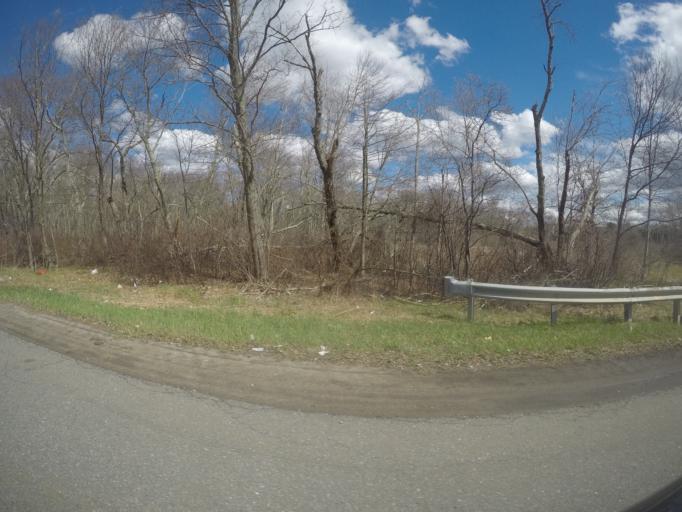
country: US
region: Massachusetts
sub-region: Bristol County
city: Raynham
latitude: 41.9871
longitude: -71.0705
